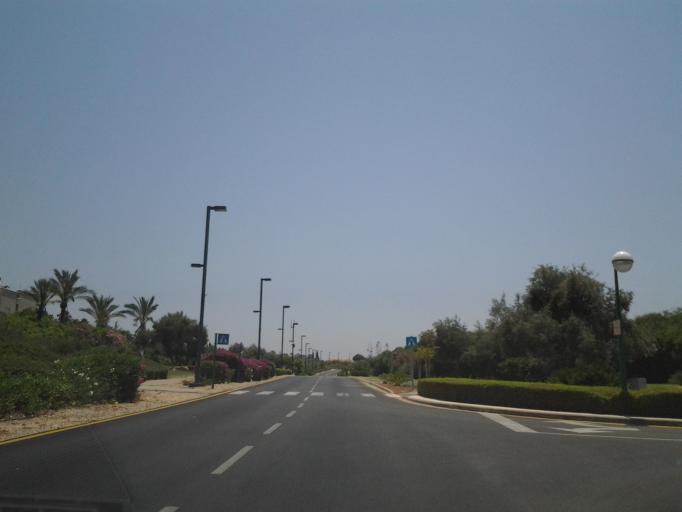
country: IL
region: Haifa
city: Qesarya
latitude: 32.5281
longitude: 34.9075
